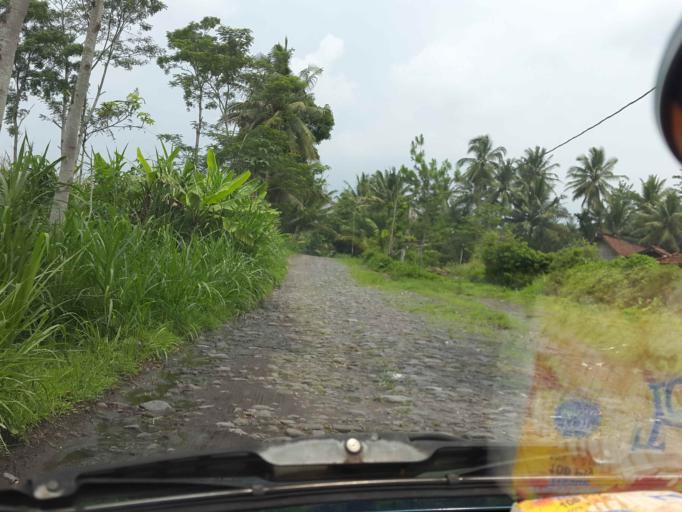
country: ID
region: Central Java
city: Muntilan
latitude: -7.5982
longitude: 110.3127
